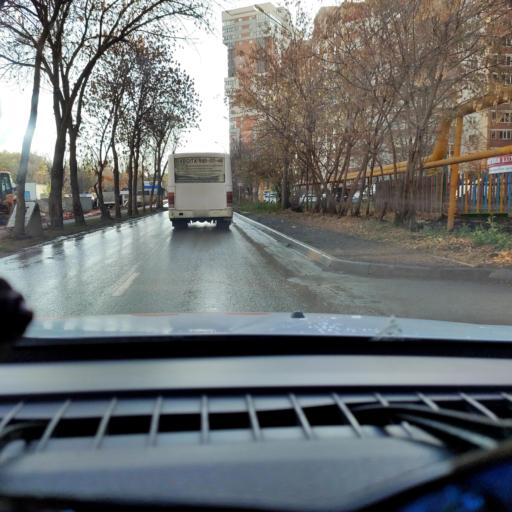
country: RU
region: Samara
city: Samara
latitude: 53.2395
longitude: 50.1792
